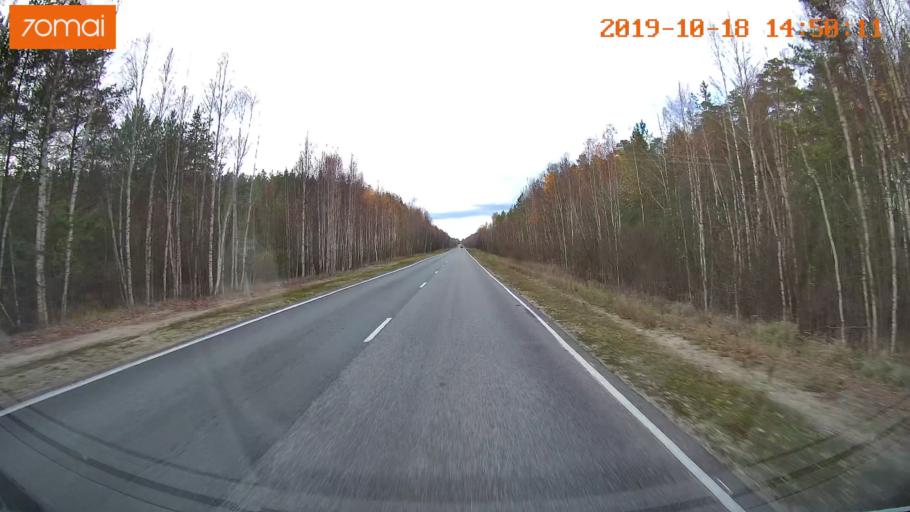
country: RU
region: Vladimir
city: Kurlovo
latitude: 55.4238
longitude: 40.6447
